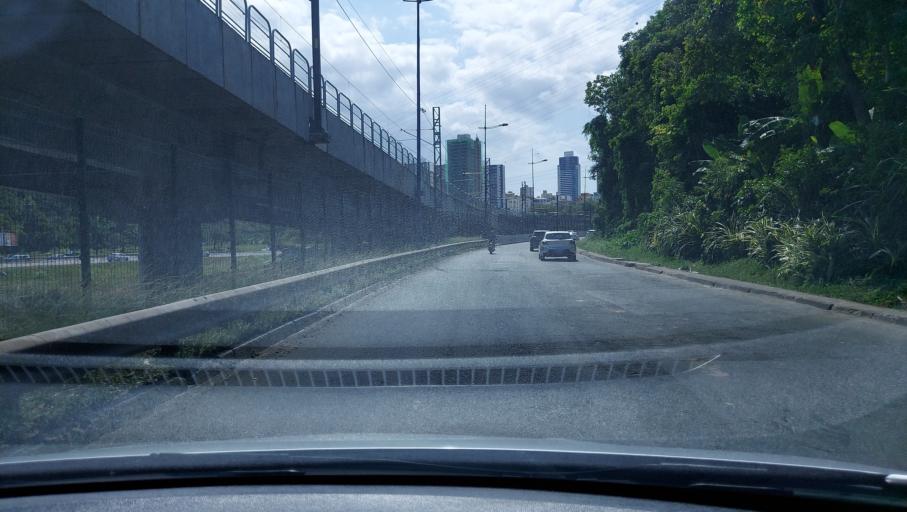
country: BR
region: Bahia
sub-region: Salvador
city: Salvador
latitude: -12.9769
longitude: -38.4739
